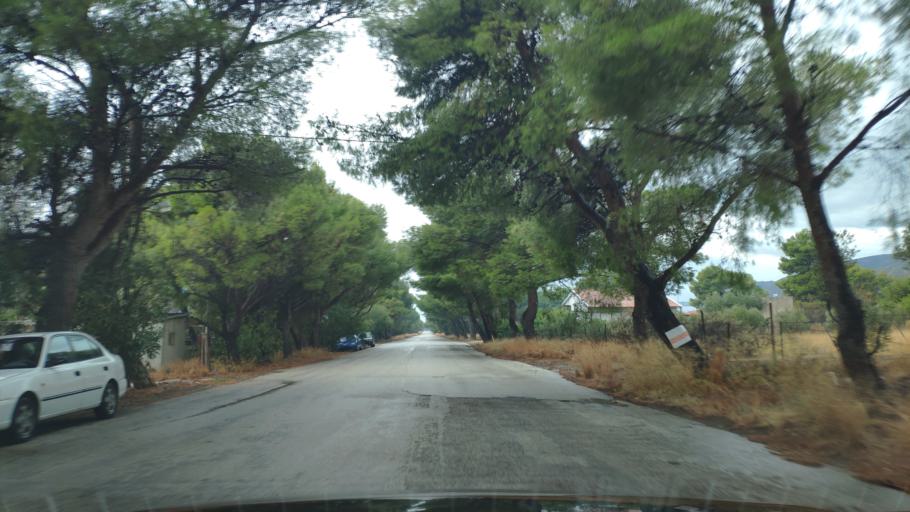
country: GR
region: Peloponnese
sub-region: Nomos Korinthias
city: Loutraki
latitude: 37.9643
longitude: 22.9960
